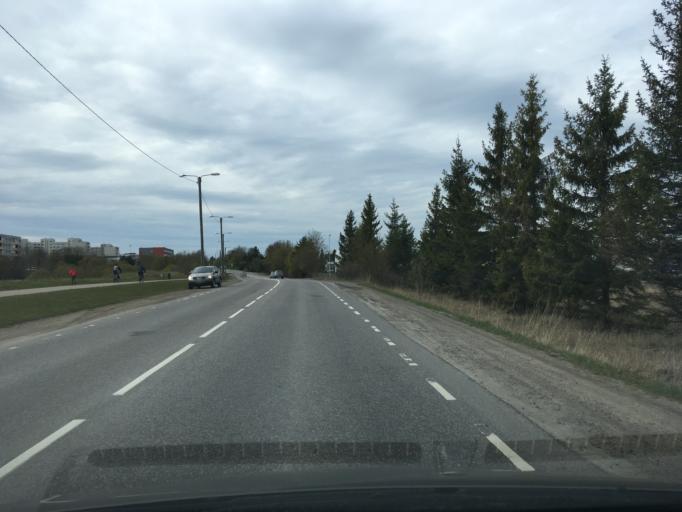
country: EE
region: Harju
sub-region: Tallinna linn
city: Kose
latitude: 59.4546
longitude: 24.8897
